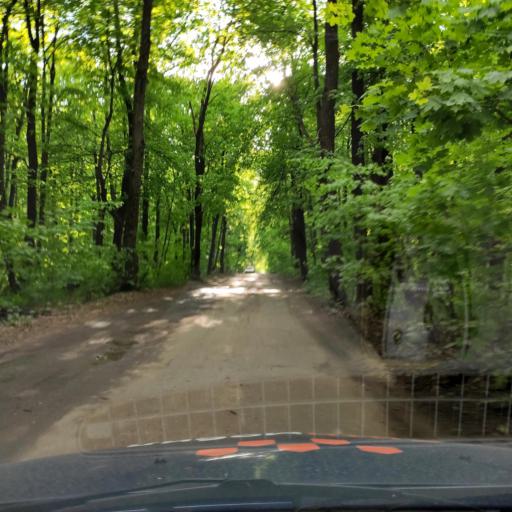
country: RU
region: Voronezj
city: Podgornoye
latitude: 51.7439
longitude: 39.2116
